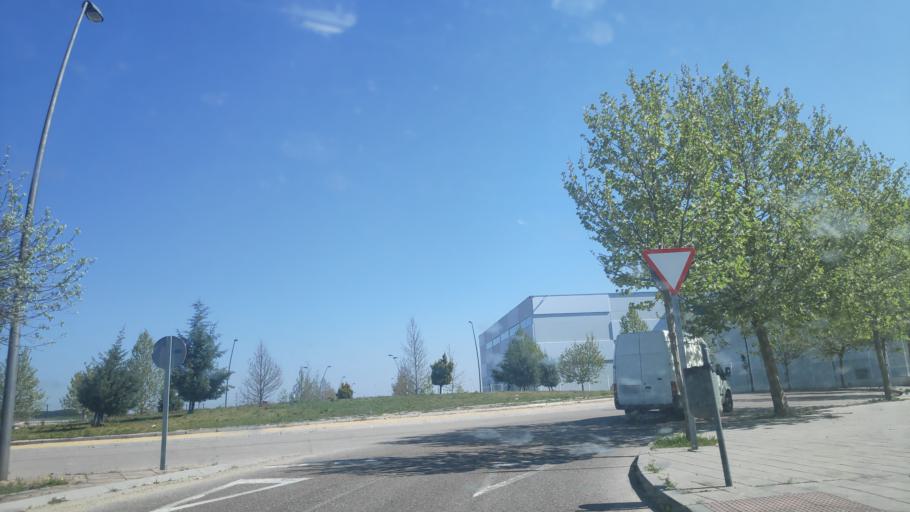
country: ES
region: Madrid
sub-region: Provincia de Madrid
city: Pinto
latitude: 40.2870
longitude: -3.6825
